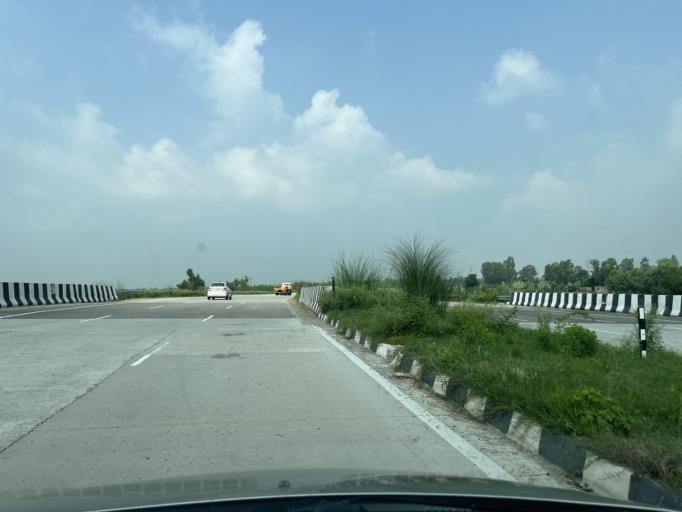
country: IN
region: Uttarakhand
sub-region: Udham Singh Nagar
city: Kashipur
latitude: 29.1632
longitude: 78.9651
